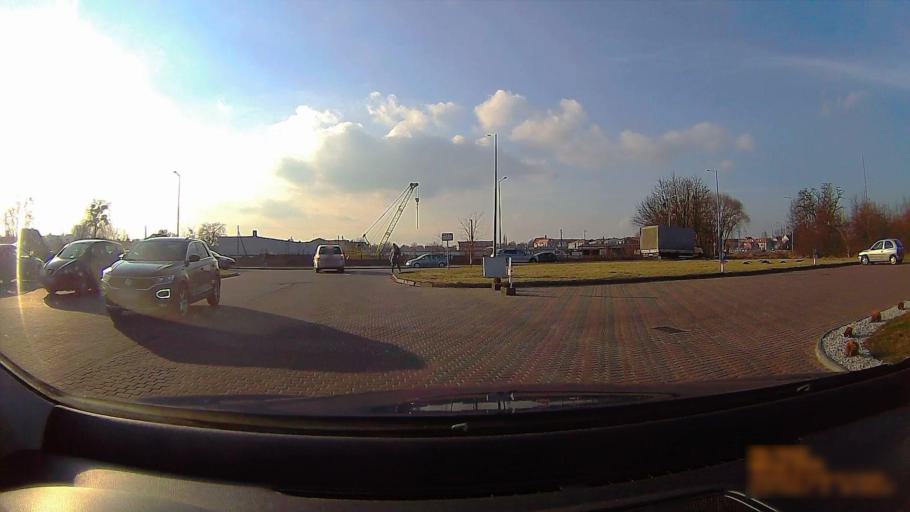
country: PL
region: Greater Poland Voivodeship
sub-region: Konin
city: Konin
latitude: 52.2081
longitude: 18.2630
